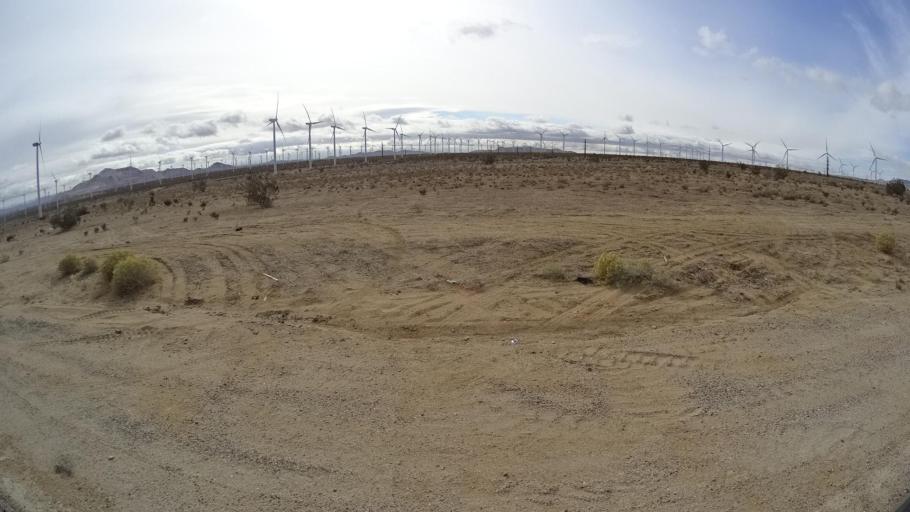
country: US
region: California
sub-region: Kern County
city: Mojave
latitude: 35.0385
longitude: -118.2596
